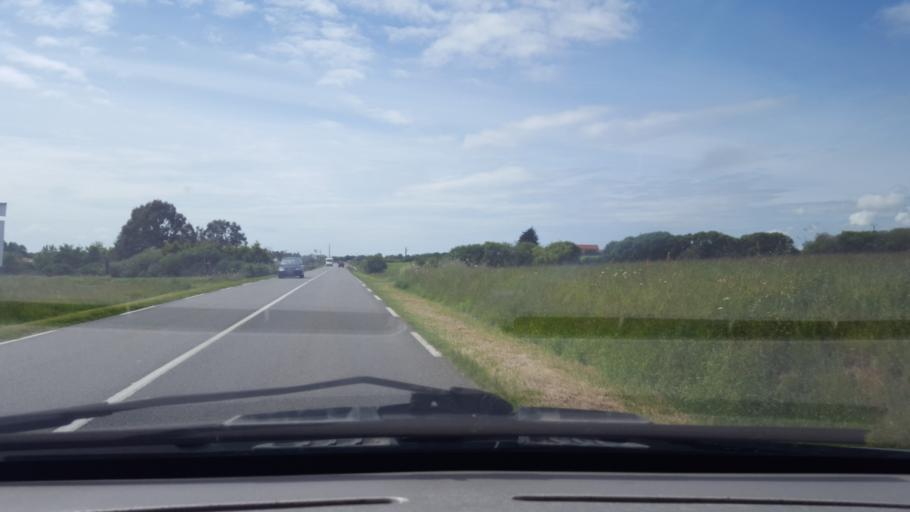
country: FR
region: Pays de la Loire
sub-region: Departement de la Loire-Atlantique
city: Bourgneuf-en-Retz
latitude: 47.0321
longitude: -1.9215
